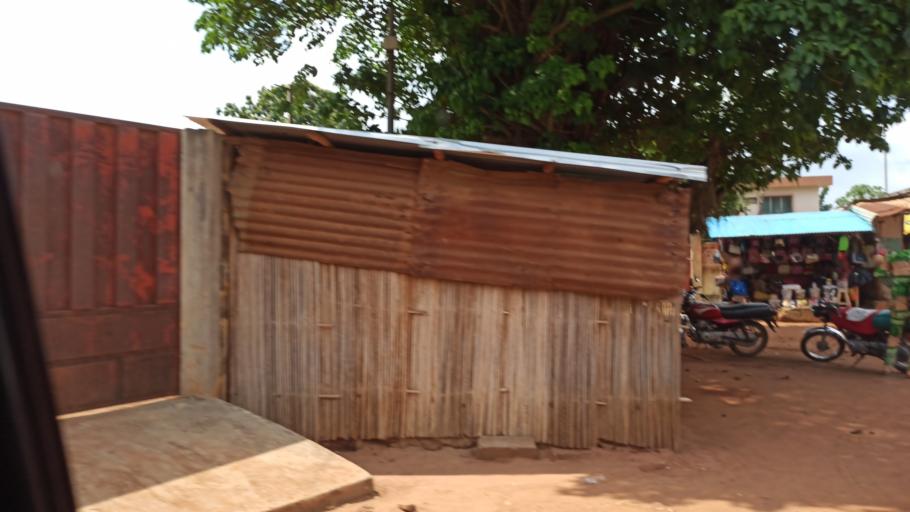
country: BJ
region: Queme
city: Porto-Novo
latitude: 6.4811
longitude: 2.6133
